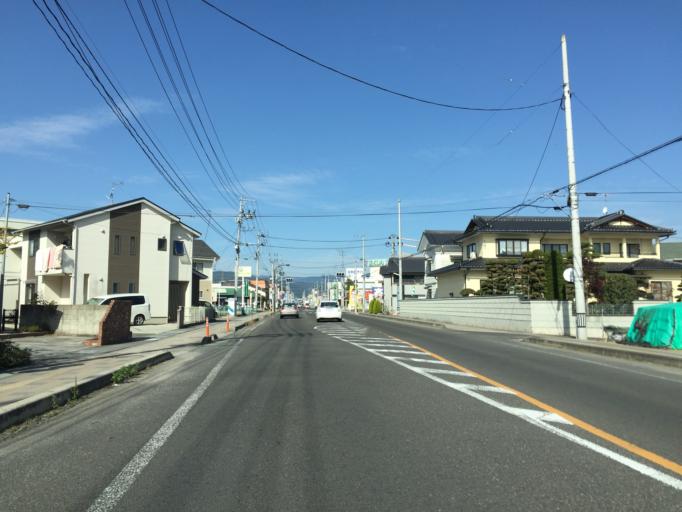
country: JP
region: Fukushima
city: Fukushima-shi
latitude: 37.7700
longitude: 140.4525
